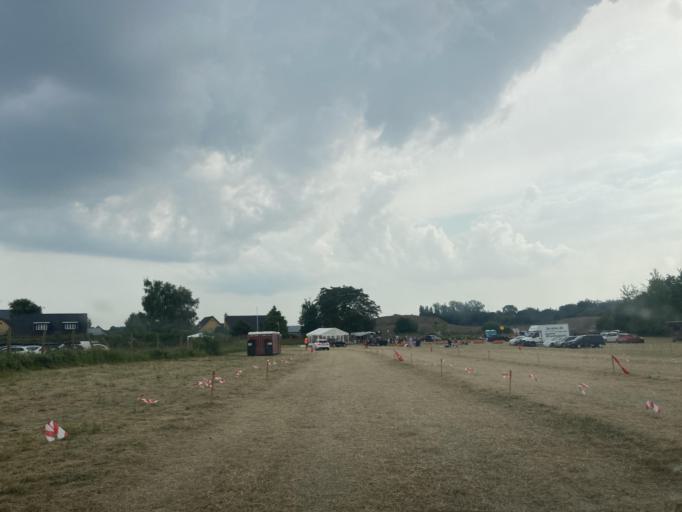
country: DK
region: Zealand
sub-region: Roskilde Kommune
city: Vindinge
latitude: 55.6135
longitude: 12.1044
